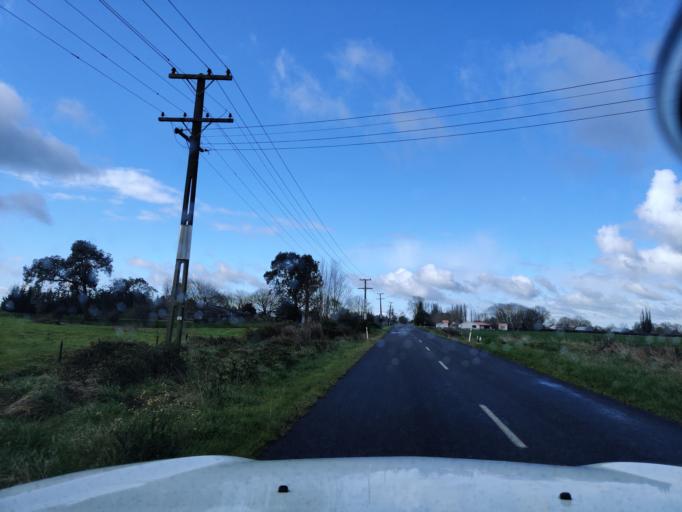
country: NZ
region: Waikato
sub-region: Waikato District
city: Ngaruawahia
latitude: -37.5719
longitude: 175.2655
